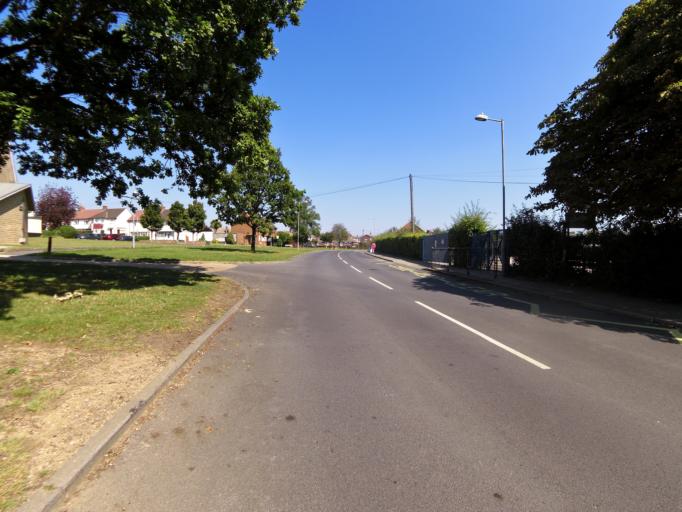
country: GB
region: England
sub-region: Suffolk
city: Ipswich
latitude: 52.0813
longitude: 1.1403
